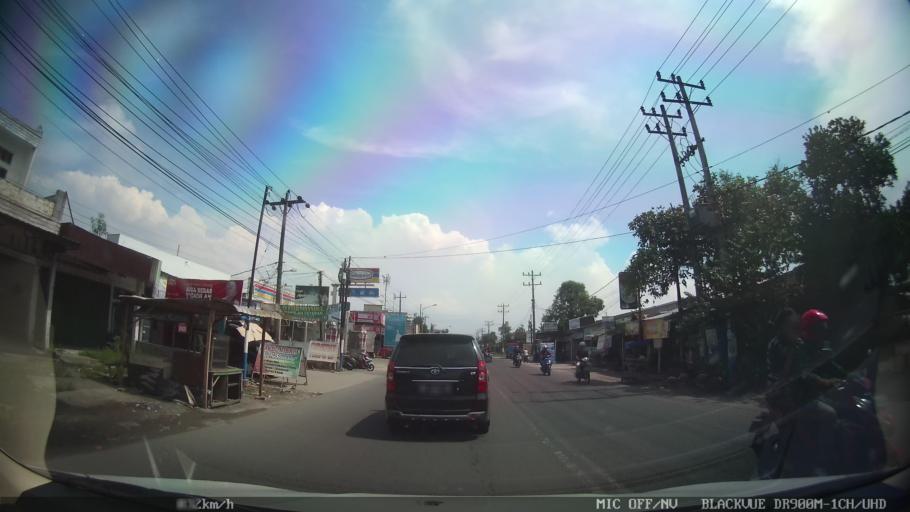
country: ID
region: North Sumatra
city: Labuhan Deli
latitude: 3.6608
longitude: 98.6564
